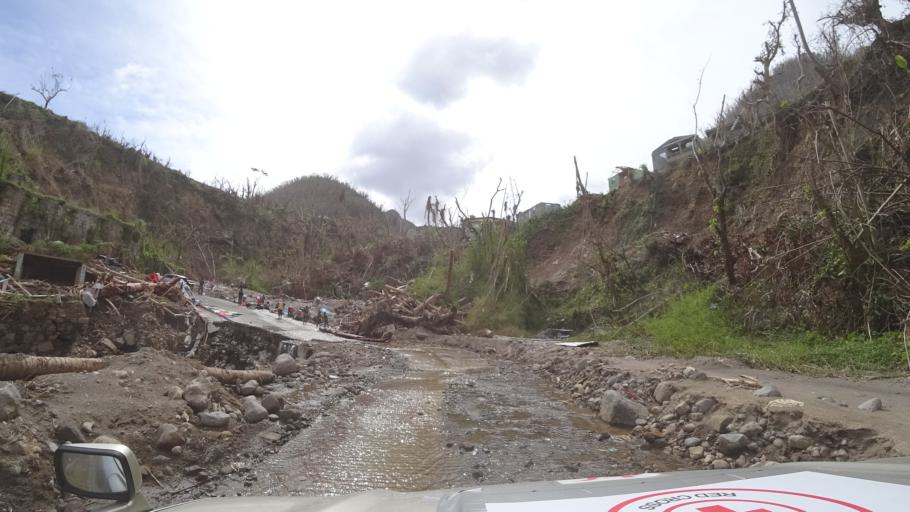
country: DM
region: Saint Patrick
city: Berekua
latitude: 15.2377
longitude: -61.3252
